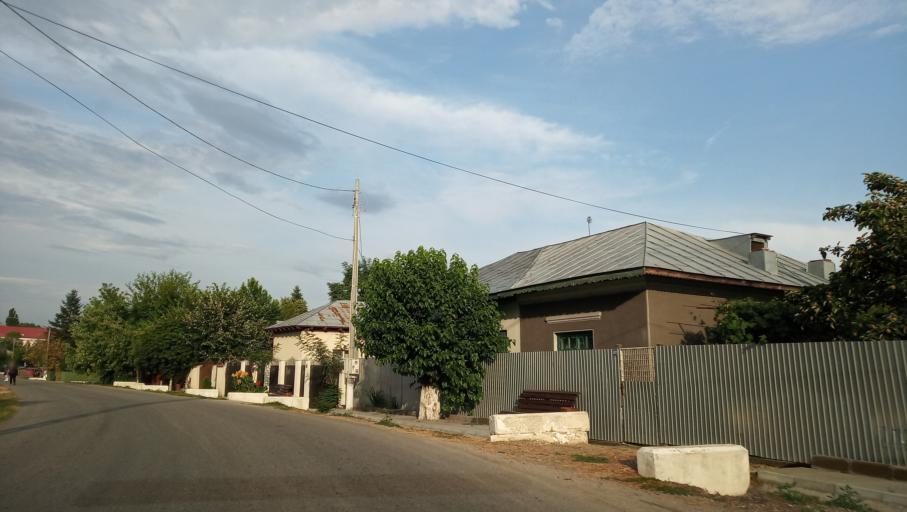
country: RO
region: Giurgiu
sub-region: Comuna Singureni
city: Singureni
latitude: 44.2257
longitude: 25.9485
